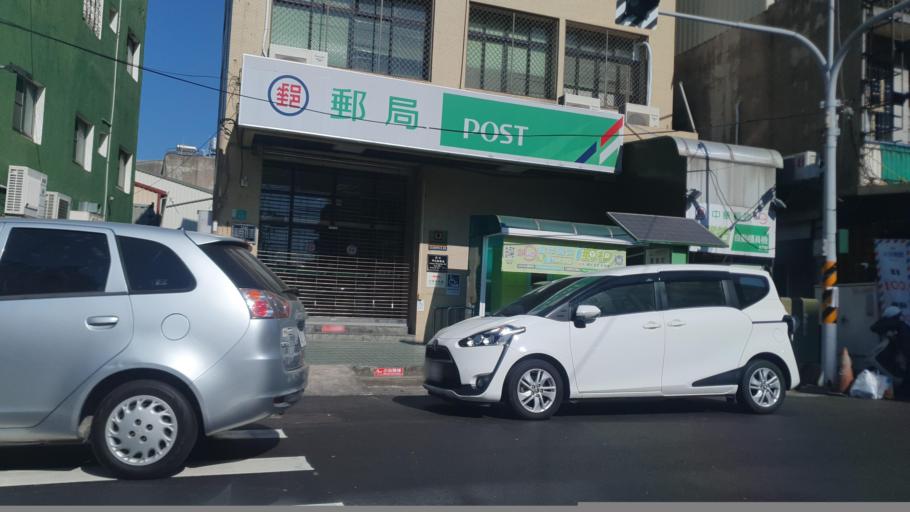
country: TW
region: Taiwan
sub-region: Tainan
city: Tainan
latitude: 23.0359
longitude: 120.3064
